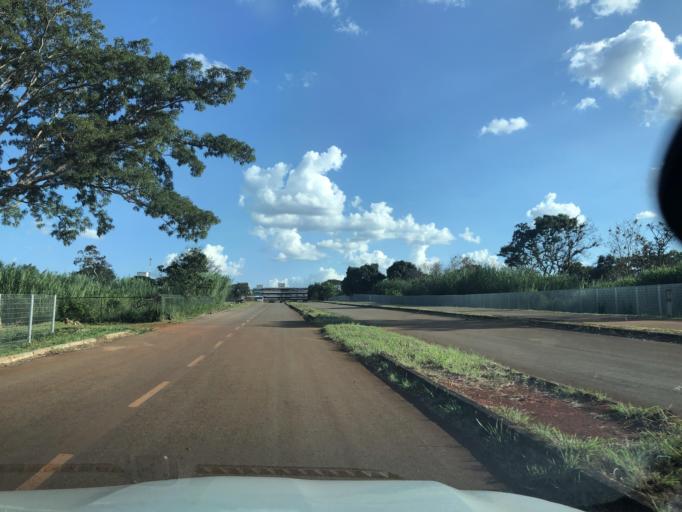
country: BR
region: Federal District
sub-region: Brasilia
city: Brasilia
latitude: -15.7396
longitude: -47.9049
